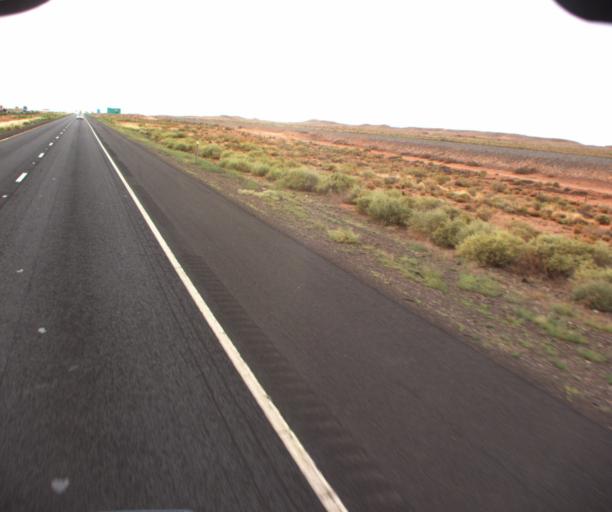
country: US
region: Arizona
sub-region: Coconino County
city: LeChee
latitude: 35.0468
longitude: -110.7657
